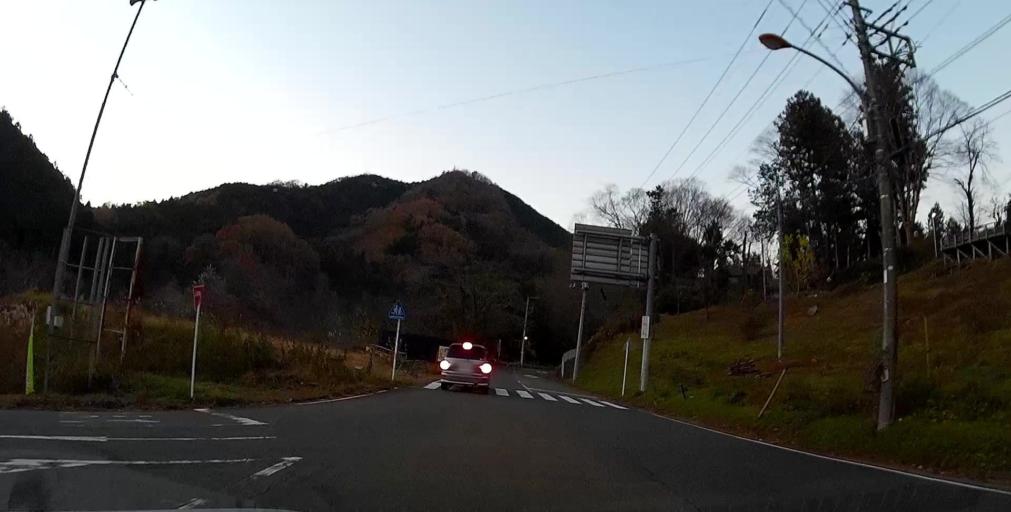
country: JP
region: Yamanashi
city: Uenohara
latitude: 35.5932
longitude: 139.1721
